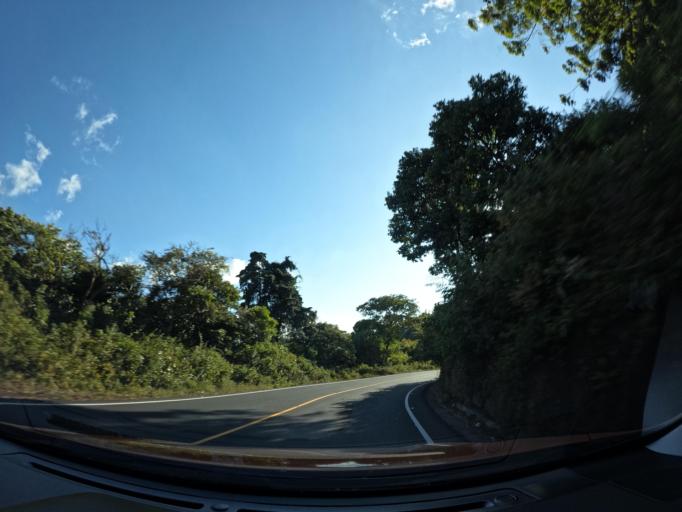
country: GT
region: Escuintla
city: Palin
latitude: 14.4426
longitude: -90.6937
